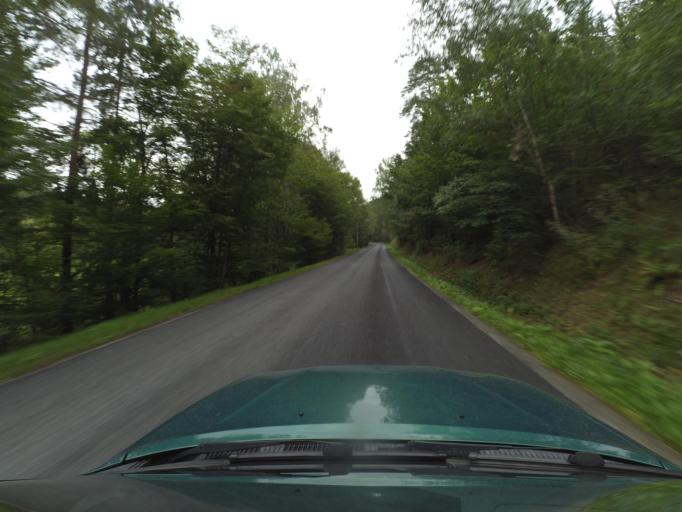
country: CZ
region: Plzensky
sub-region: Okres Plzen-Sever
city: Tremosna
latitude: 49.8280
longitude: 13.4076
